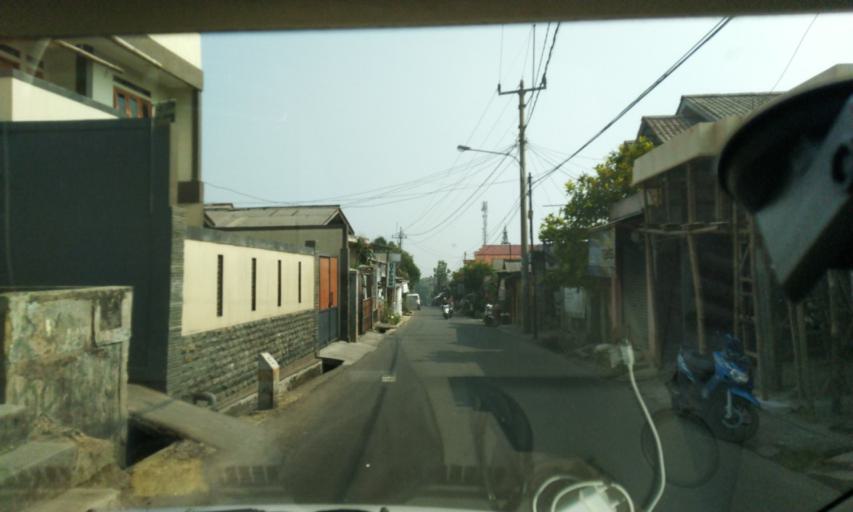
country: ID
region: West Java
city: Caringin
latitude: -6.6688
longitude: 106.8670
